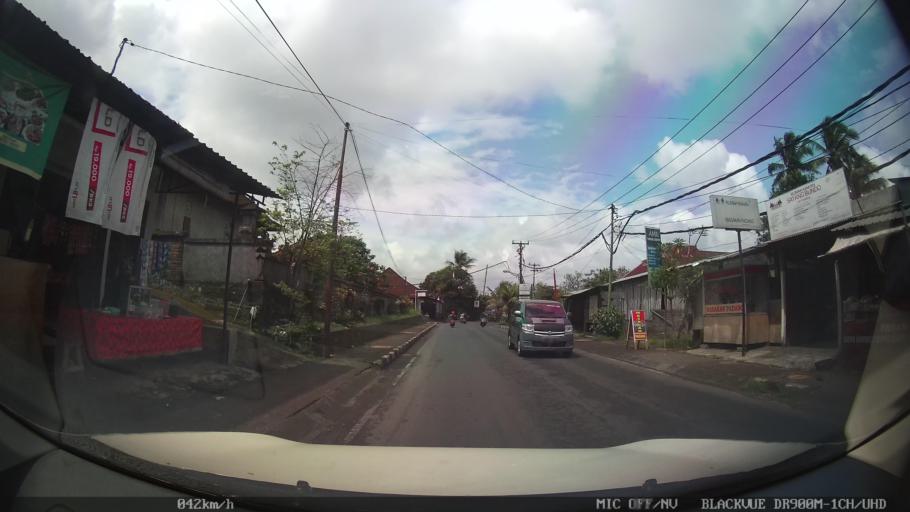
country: ID
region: Bali
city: Banjar Cemenggon
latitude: -8.5482
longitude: 115.1980
